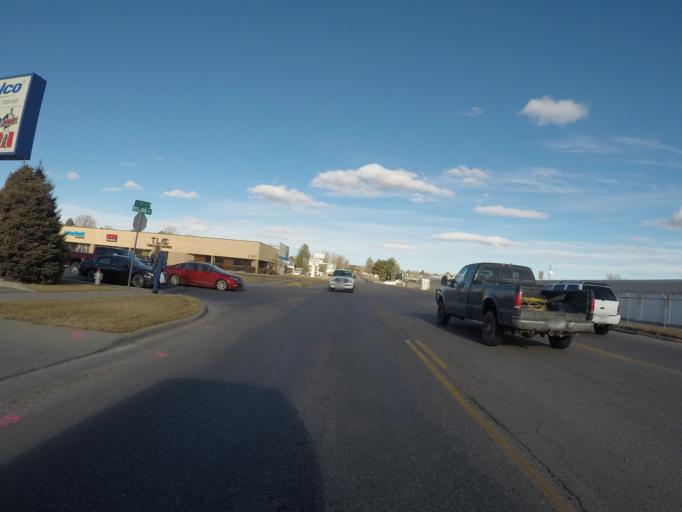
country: US
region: Montana
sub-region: Yellowstone County
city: Billings
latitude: 45.7585
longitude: -108.5667
